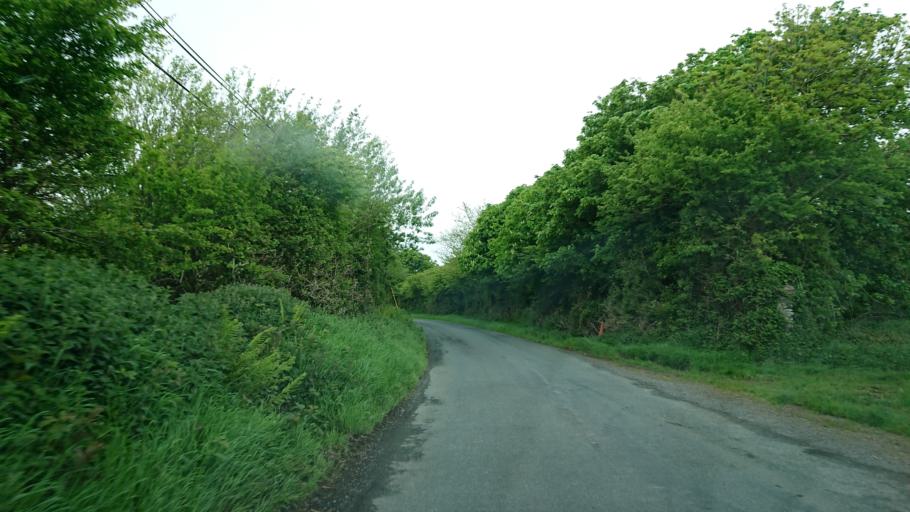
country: IE
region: Munster
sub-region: Waterford
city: Waterford
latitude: 52.2220
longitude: -7.0352
